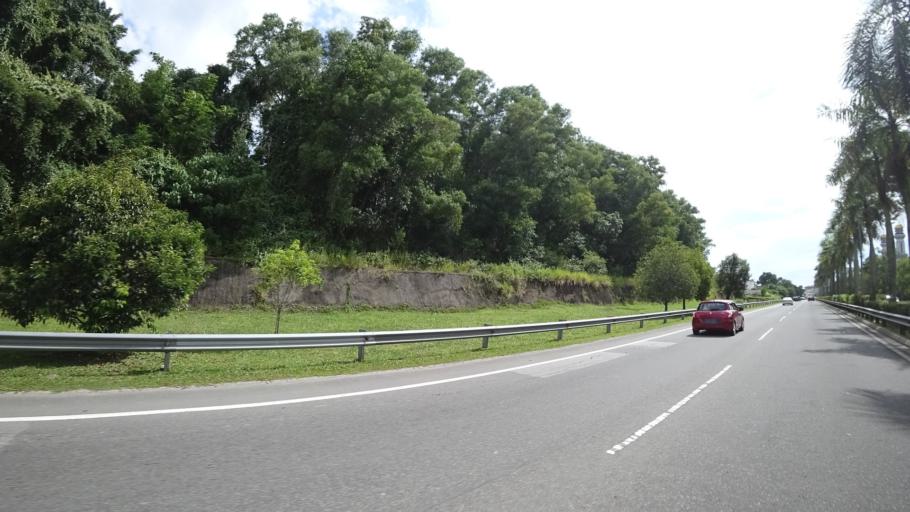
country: BN
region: Brunei and Muara
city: Bandar Seri Begawan
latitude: 4.8957
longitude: 114.9248
